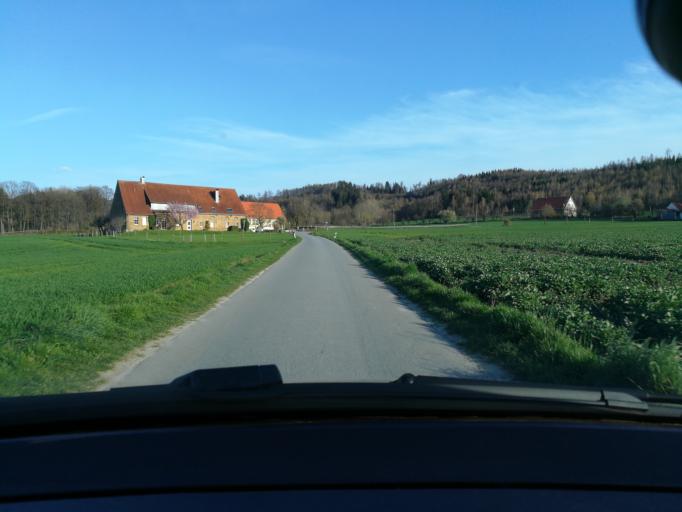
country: DE
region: North Rhine-Westphalia
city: Borgholzhausen
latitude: 52.0918
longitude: 8.3069
